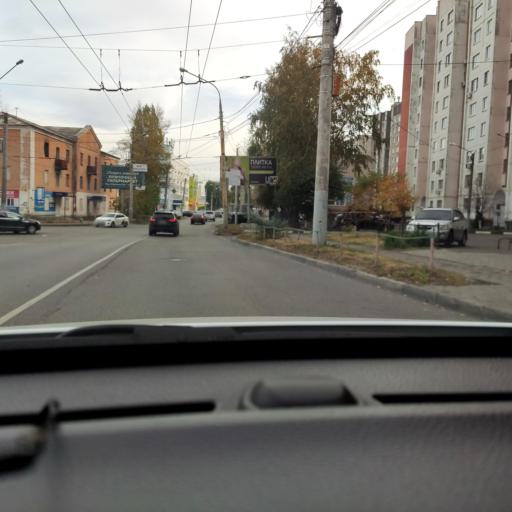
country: RU
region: Voronezj
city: Voronezh
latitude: 51.6632
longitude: 39.1584
